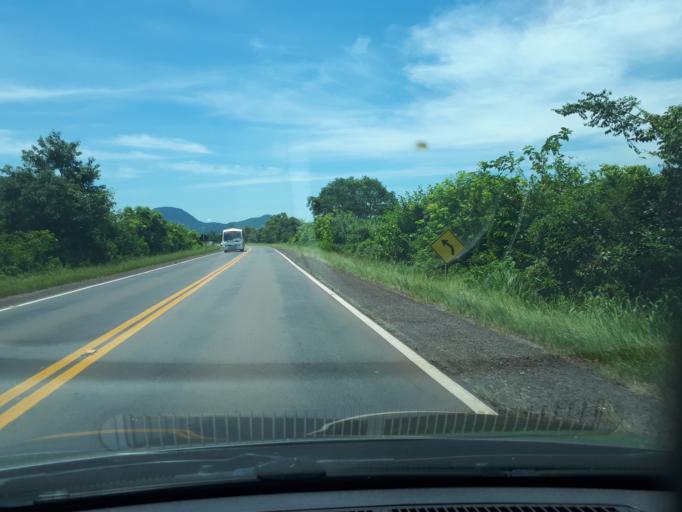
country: BR
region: Rio Grande do Sul
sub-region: Candelaria
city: Candelaria
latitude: -29.7247
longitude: -52.9242
